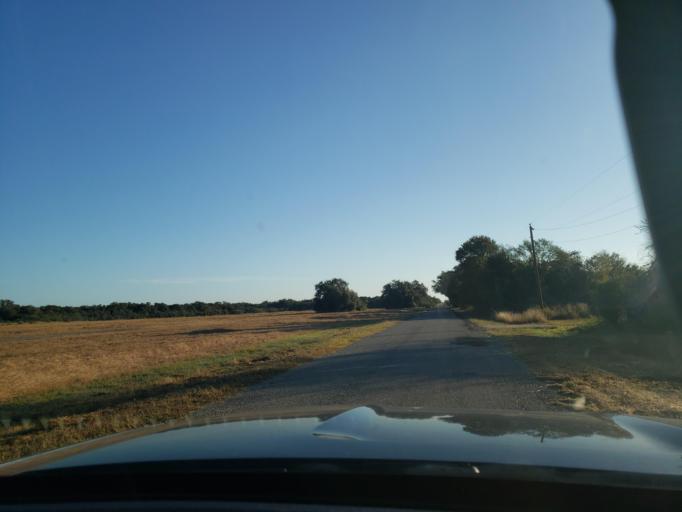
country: US
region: Texas
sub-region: Bee County
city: Beeville
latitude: 28.4217
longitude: -97.7095
